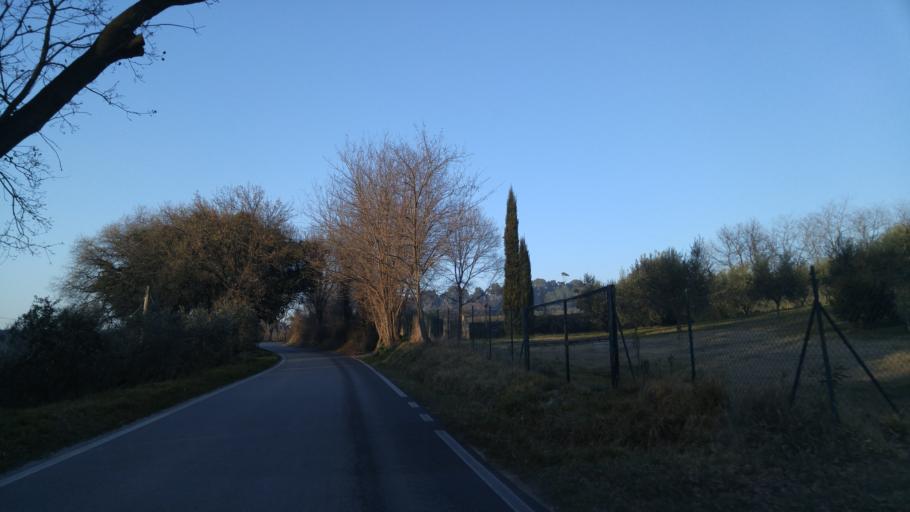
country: IT
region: The Marches
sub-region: Provincia di Pesaro e Urbino
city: Fenile
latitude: 43.8595
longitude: 12.9630
